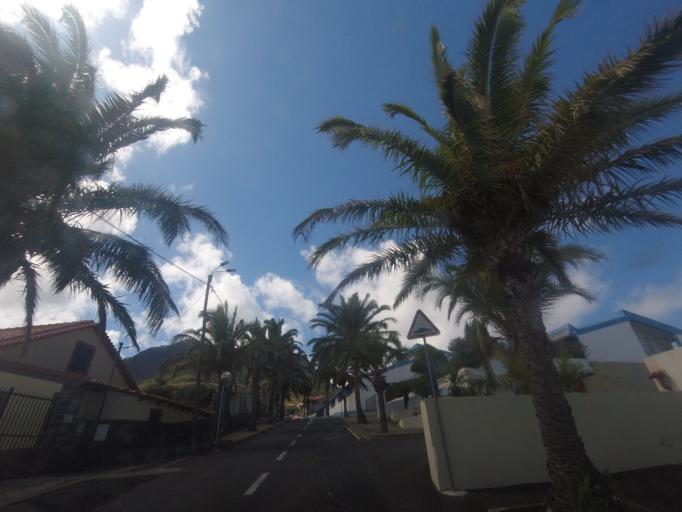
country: PT
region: Madeira
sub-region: Machico
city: Canical
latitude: 32.7366
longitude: -16.7409
